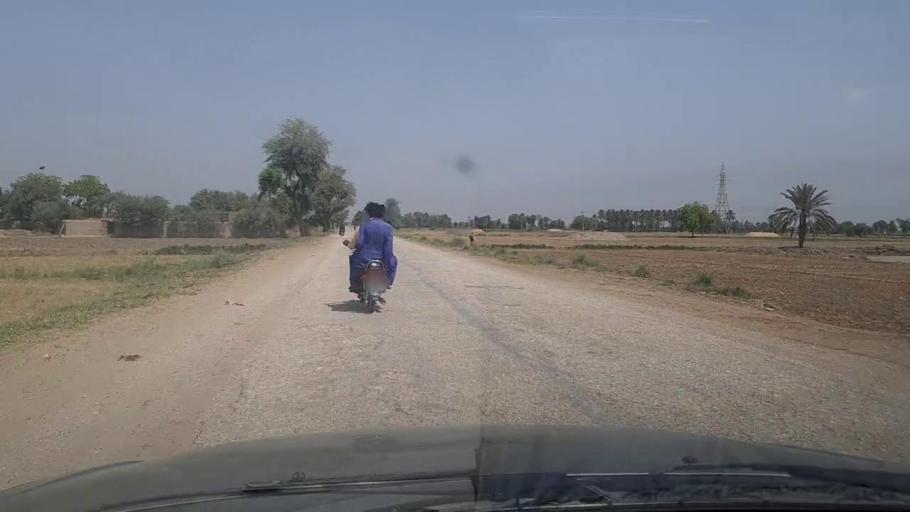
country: PK
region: Sindh
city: Setharja Old
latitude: 27.1503
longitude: 68.5234
